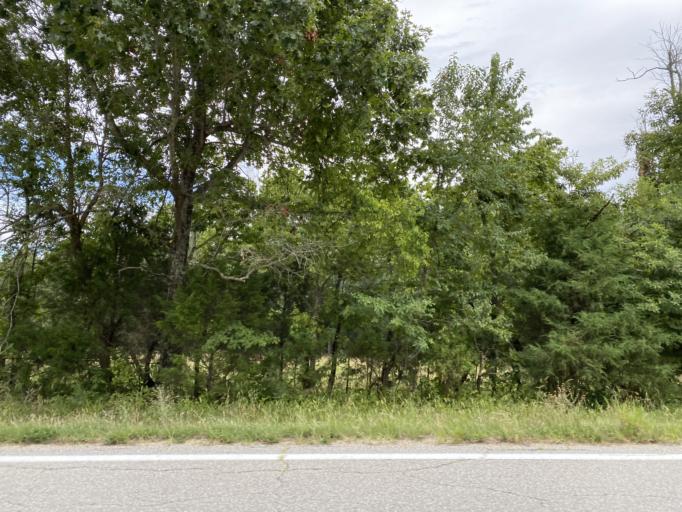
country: US
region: Arkansas
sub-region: Fulton County
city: Salem
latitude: 36.4219
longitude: -91.7124
